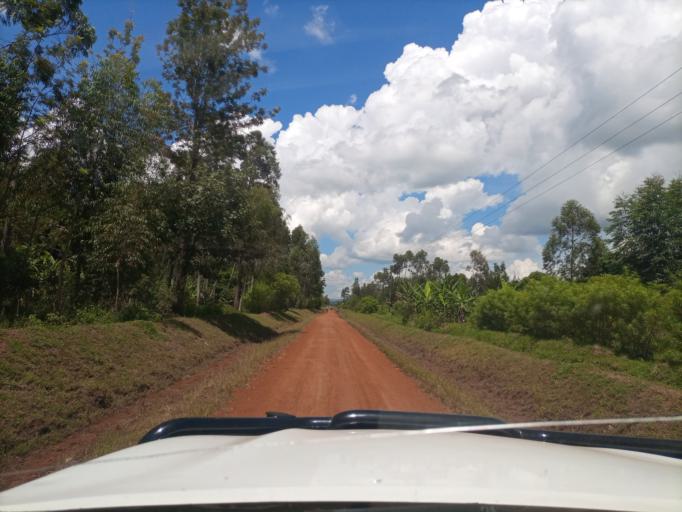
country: UG
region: Eastern Region
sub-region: Tororo District
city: Tororo
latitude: 0.6593
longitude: 34.0001
